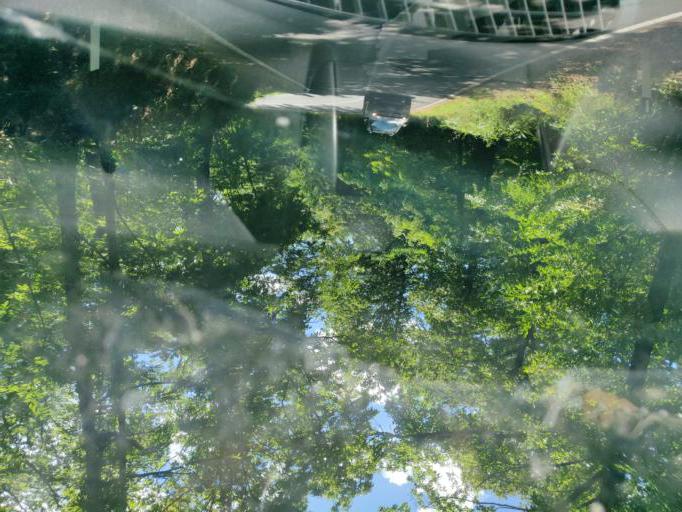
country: IT
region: Tuscany
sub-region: Provincia di Siena
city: Abbadia San Salvatore
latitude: 42.8873
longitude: 11.6568
